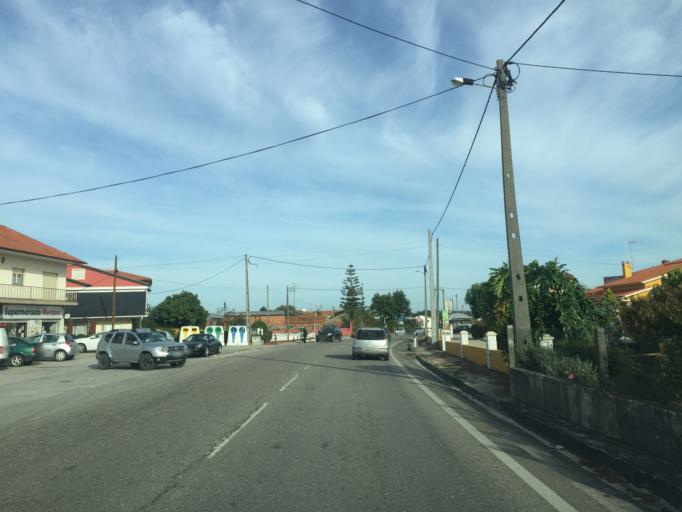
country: PT
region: Leiria
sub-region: Pombal
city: Lourical
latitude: 39.9646
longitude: -8.7908
